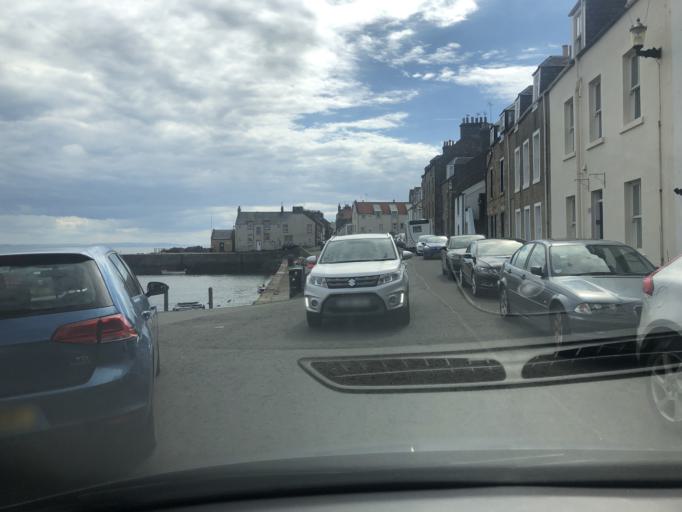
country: GB
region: Scotland
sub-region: Fife
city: Anstruther
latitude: 56.2259
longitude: -2.6829
